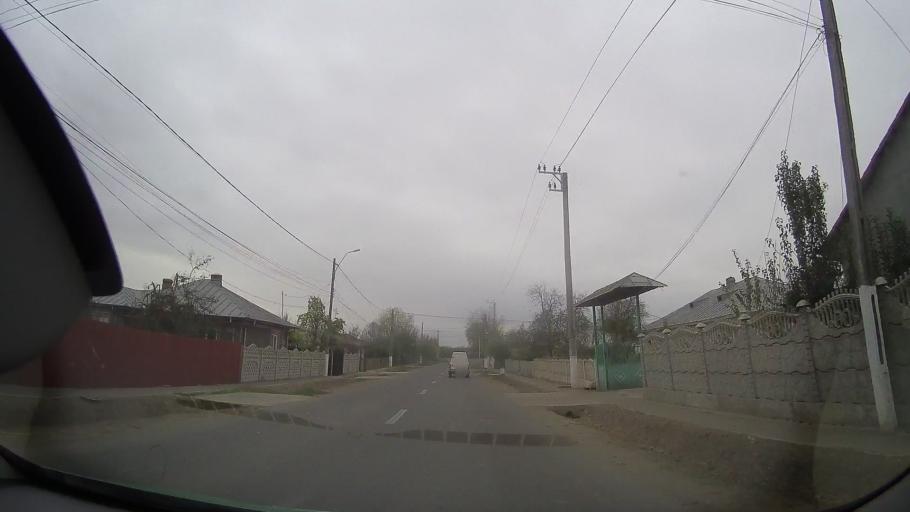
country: RO
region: Braila
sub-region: Comuna Budesti
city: Tataru
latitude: 44.8511
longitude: 27.4249
